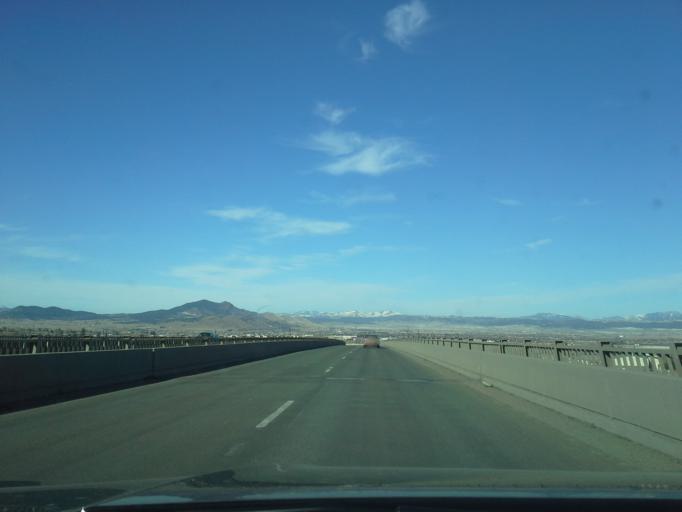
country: US
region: Montana
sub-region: Lewis and Clark County
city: Helena
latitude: 46.5980
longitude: -112.0027
